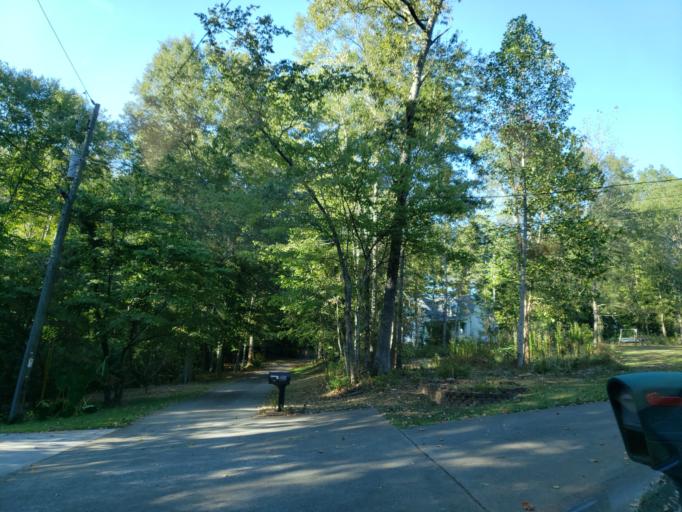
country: US
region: Georgia
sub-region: Cherokee County
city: Ball Ground
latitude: 34.3385
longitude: -84.3845
